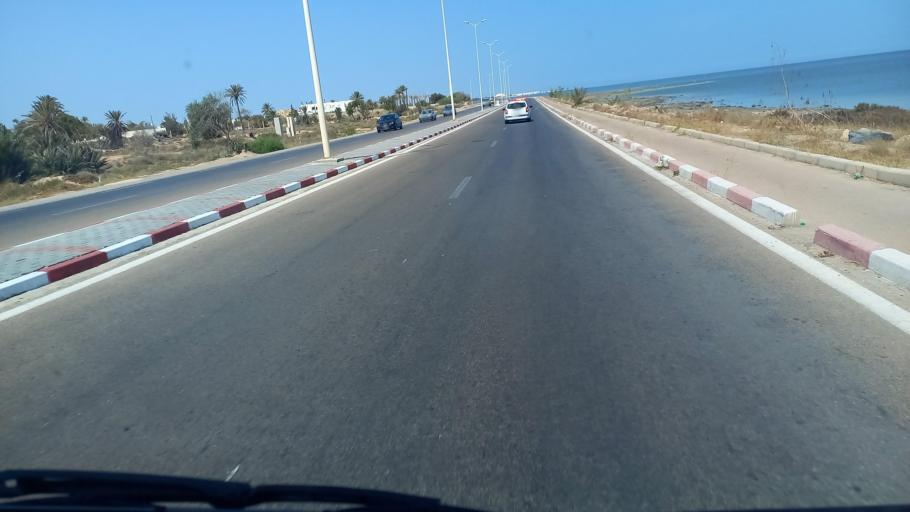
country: TN
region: Madanin
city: Houmt Souk
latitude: 33.8740
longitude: 10.9069
